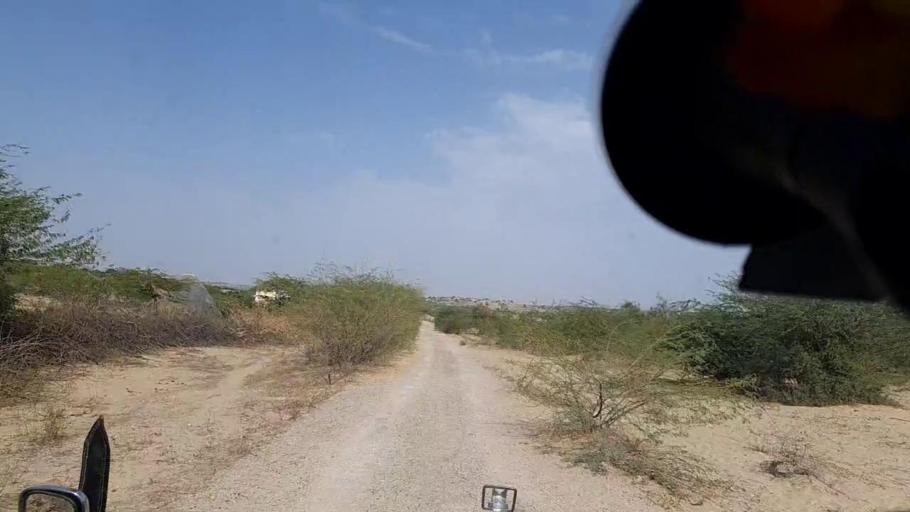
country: PK
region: Sindh
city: Diplo
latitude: 24.4332
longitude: 69.4314
